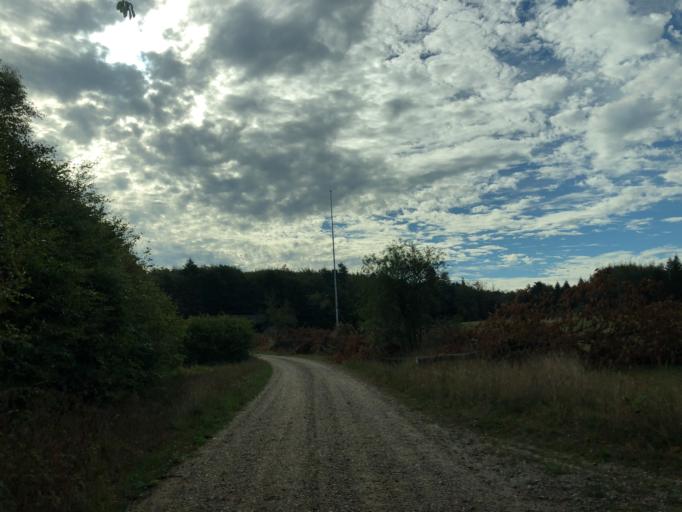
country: DK
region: Central Jutland
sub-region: Holstebro Kommune
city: Ulfborg
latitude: 56.1632
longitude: 8.4039
